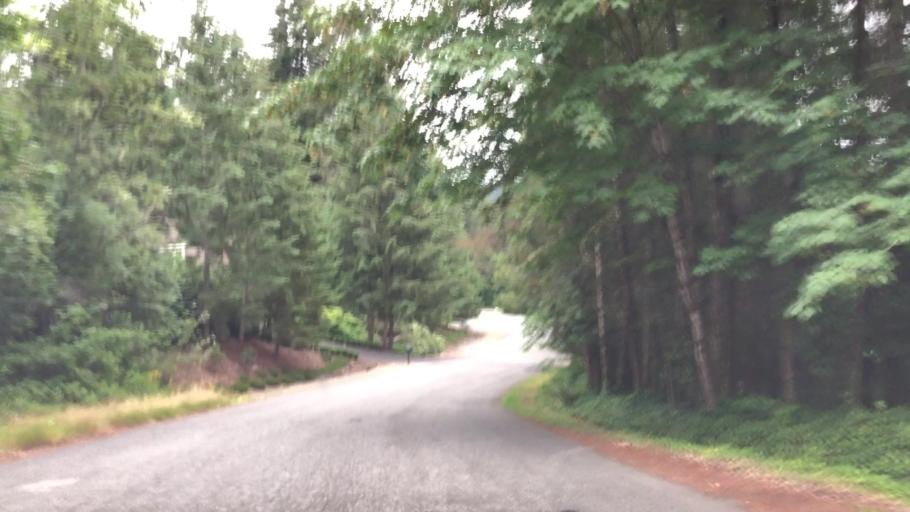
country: US
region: Washington
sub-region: King County
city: Cottage Lake
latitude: 47.7184
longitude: -122.0932
